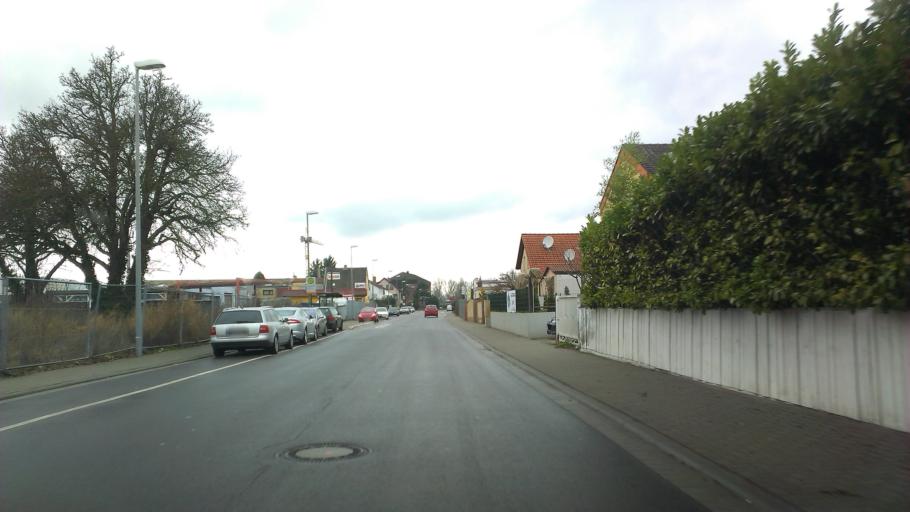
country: DE
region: Rheinland-Pfalz
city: Frankenthal
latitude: 49.4965
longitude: 8.3753
